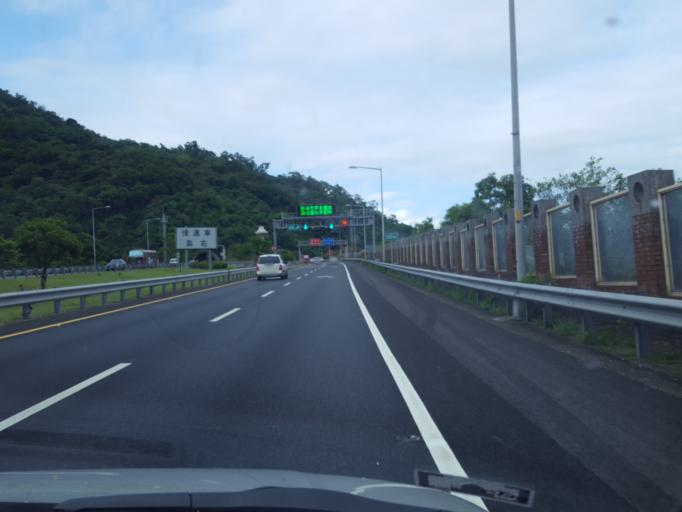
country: TW
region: Taiwan
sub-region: Yilan
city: Yilan
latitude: 24.8448
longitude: 121.7901
